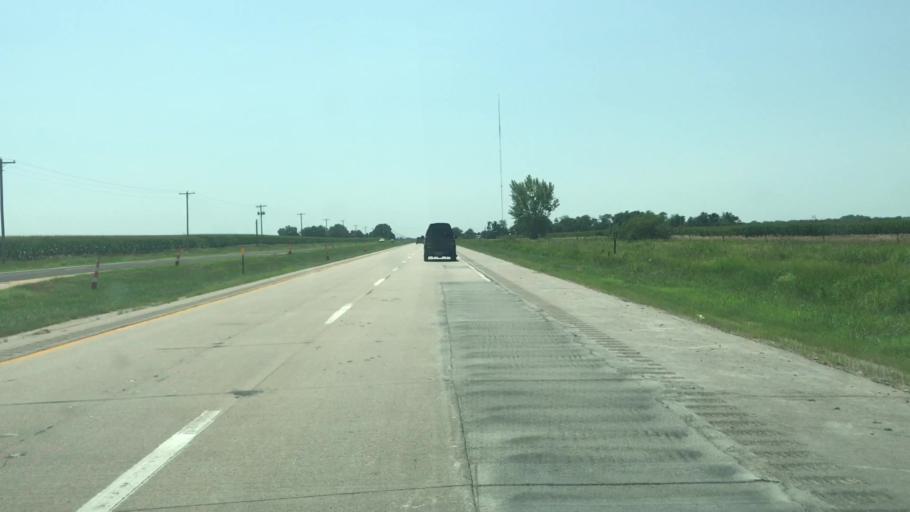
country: US
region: Nebraska
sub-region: Adams County
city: Hastings
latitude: 40.6620
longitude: -98.3824
